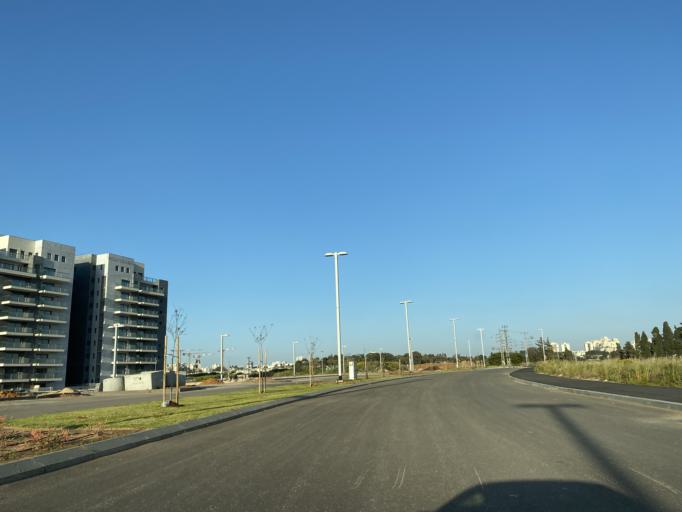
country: IL
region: Tel Aviv
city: Herzliyya
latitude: 32.1559
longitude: 34.8203
